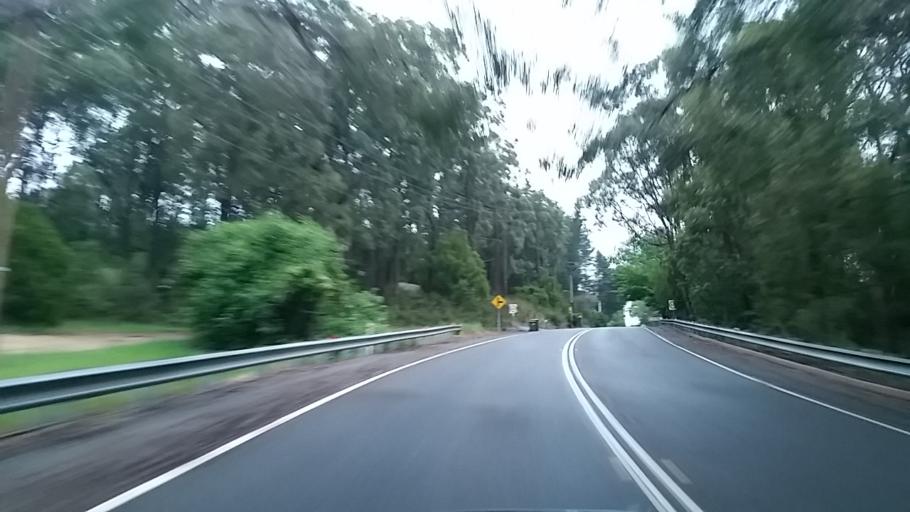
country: AU
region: South Australia
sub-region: Adelaide Hills
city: Crafers
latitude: -34.9894
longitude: 138.7079
